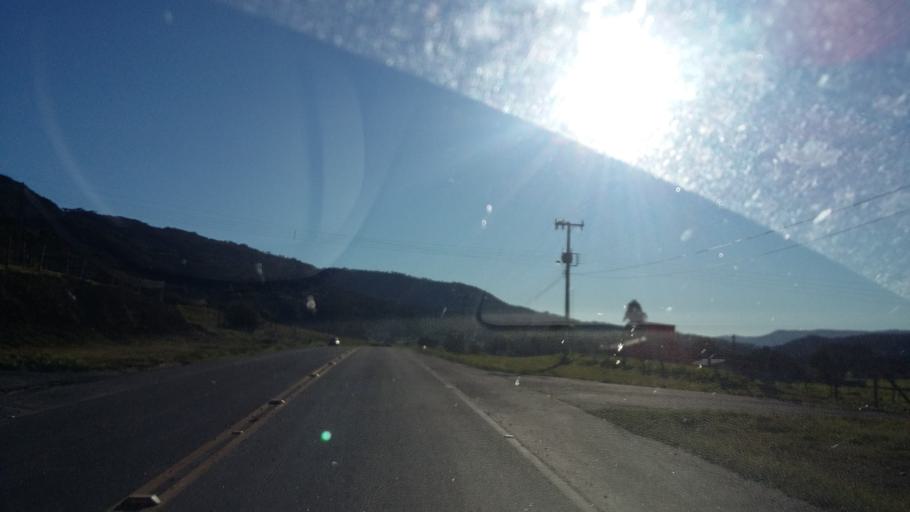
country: BR
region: Santa Catarina
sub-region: Lauro Muller
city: Lauro Muller
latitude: -28.0194
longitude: -49.5152
